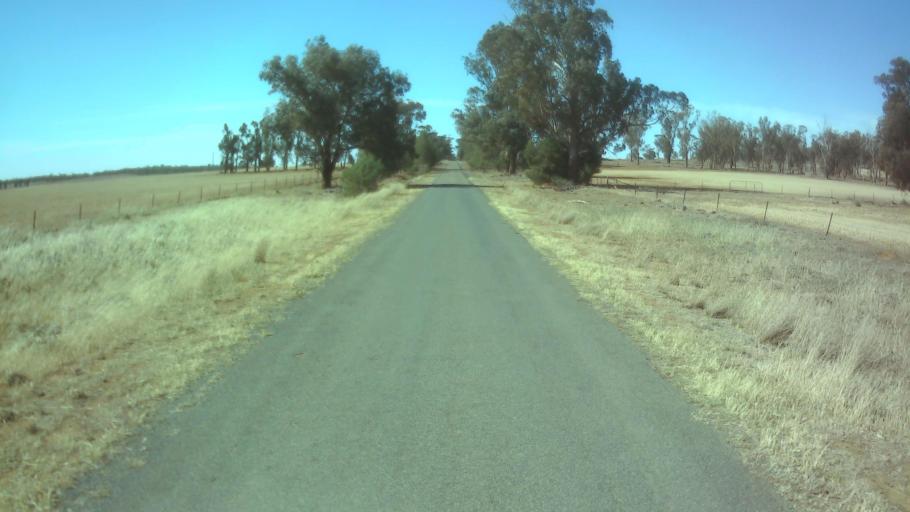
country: AU
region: New South Wales
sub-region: Forbes
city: Forbes
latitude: -33.7341
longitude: 147.7422
